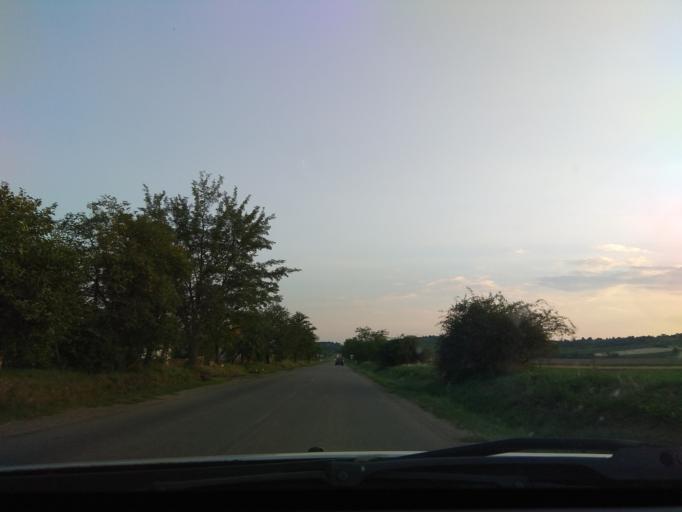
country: HU
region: Borsod-Abauj-Zemplen
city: Szerencs
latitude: 48.1842
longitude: 21.2075
